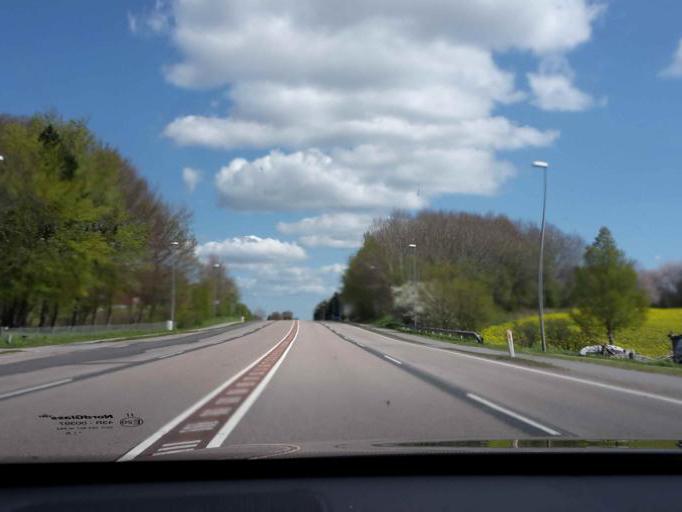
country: DK
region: South Denmark
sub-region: Assens Kommune
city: Tommerup
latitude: 55.3895
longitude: 10.2471
